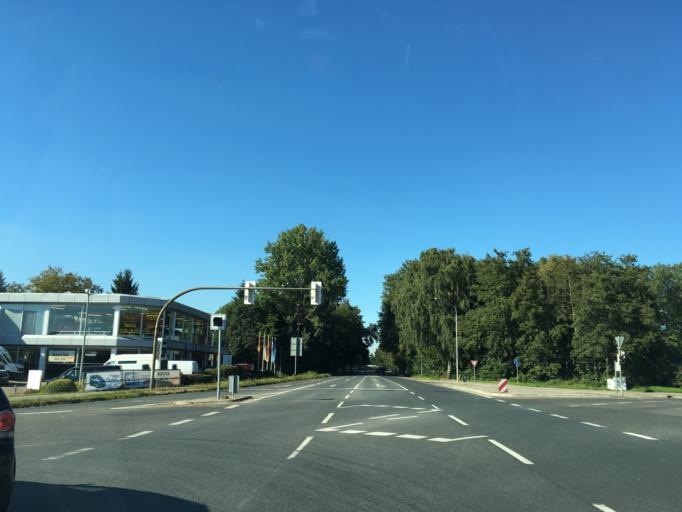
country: DE
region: Lower Saxony
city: Winsen
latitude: 53.3570
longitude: 10.2034
